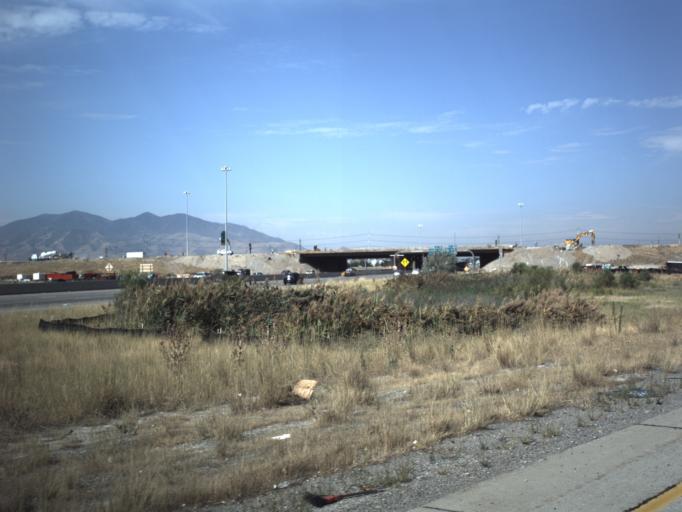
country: US
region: Utah
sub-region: Salt Lake County
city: Taylorsville
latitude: 40.7252
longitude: -111.9472
